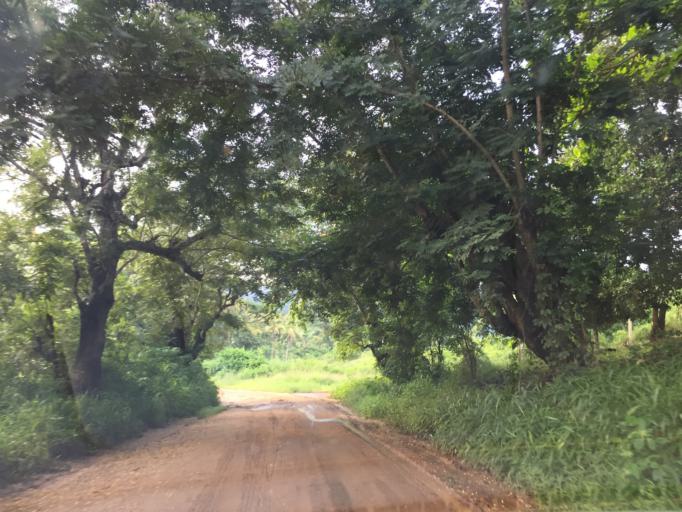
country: TZ
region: Tanga
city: Muheza
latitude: -5.1624
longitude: 38.7707
